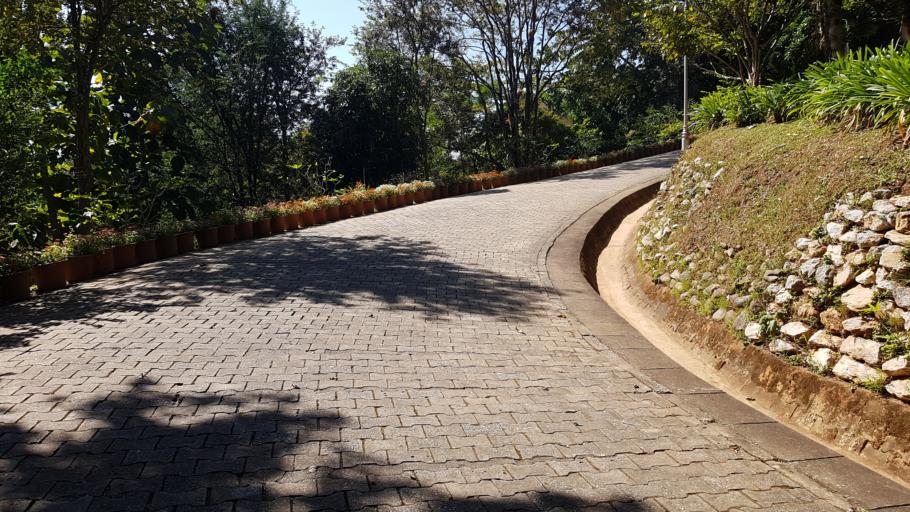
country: TH
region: Chiang Rai
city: Mae Fa Luang
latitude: 20.2870
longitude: 99.8109
